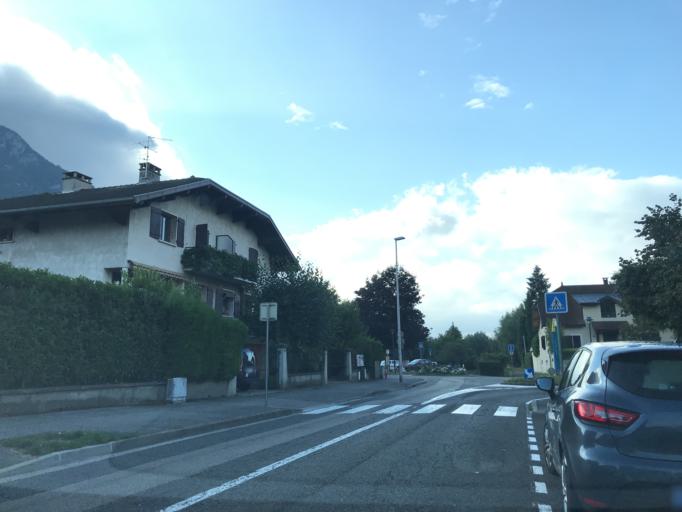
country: FR
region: Rhone-Alpes
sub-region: Departement de la Haute-Savoie
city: Annecy-le-Vieux
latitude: 45.9078
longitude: 6.1515
